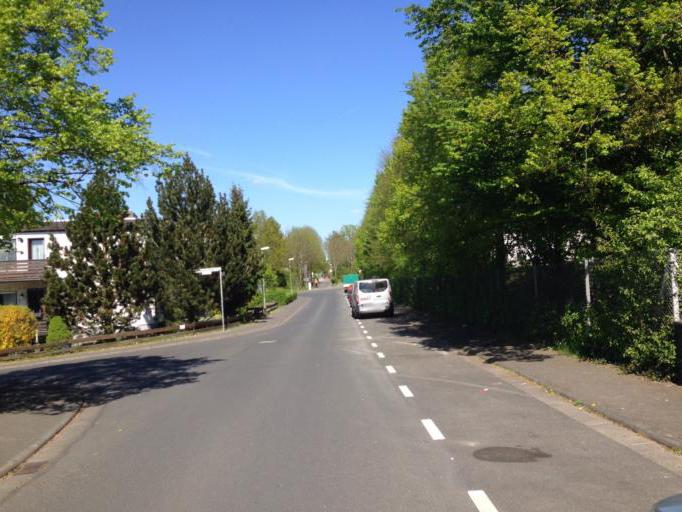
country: DE
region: Hesse
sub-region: Regierungsbezirk Giessen
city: Giessen
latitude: 50.5676
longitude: 8.6582
